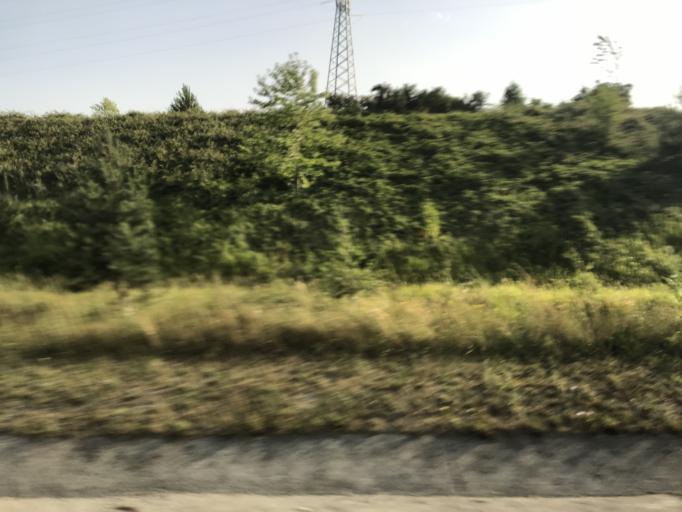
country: ES
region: Navarre
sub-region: Provincia de Navarra
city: Altsasu
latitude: 42.9175
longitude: -2.1991
